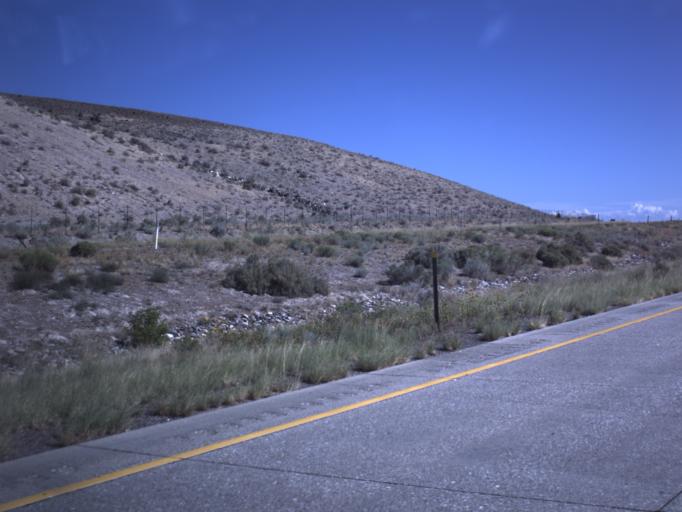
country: US
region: Utah
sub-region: Sevier County
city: Monroe
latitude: 38.6036
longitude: -112.2387
